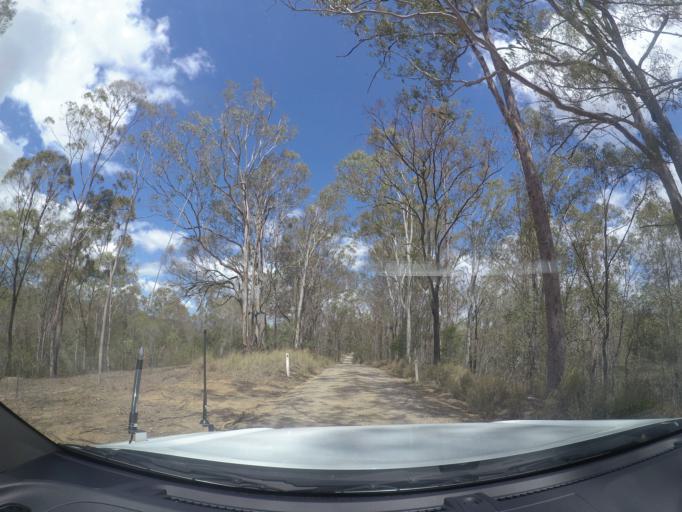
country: AU
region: Queensland
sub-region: Logan
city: Cedar Vale
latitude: -27.8983
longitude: 153.0444
